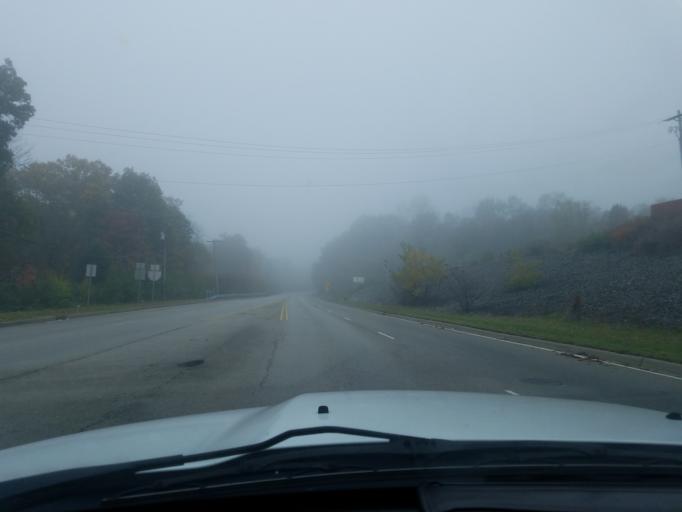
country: US
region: Indiana
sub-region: Floyd County
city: New Albany
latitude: 38.3120
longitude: -85.8471
